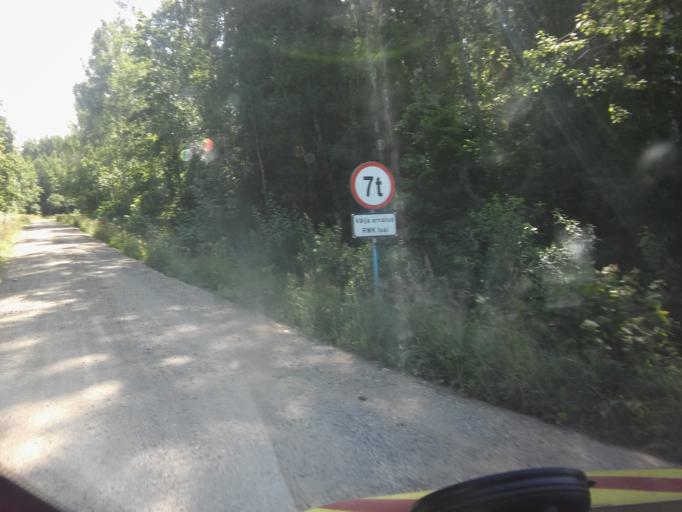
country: EE
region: Paernumaa
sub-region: Paikuse vald
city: Paikuse
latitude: 58.2913
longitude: 24.6915
